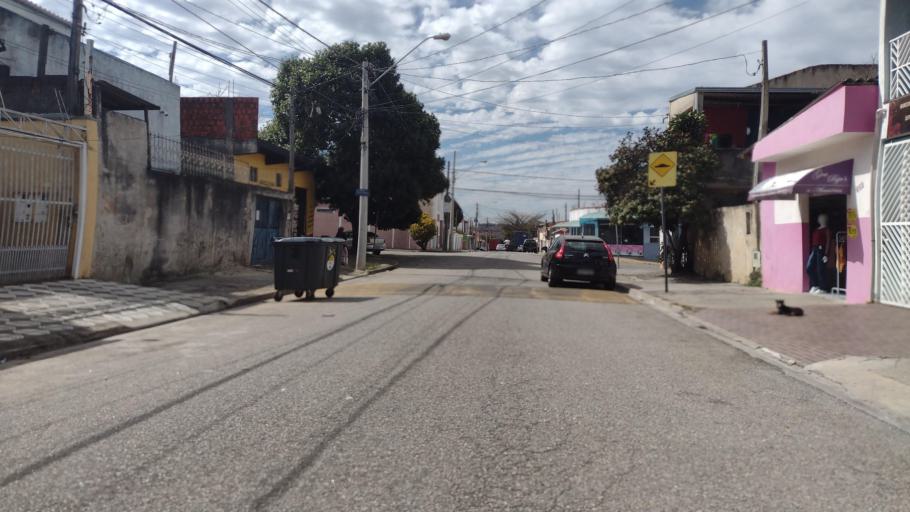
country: BR
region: Sao Paulo
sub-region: Sorocaba
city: Sorocaba
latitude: -23.4318
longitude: -47.4626
